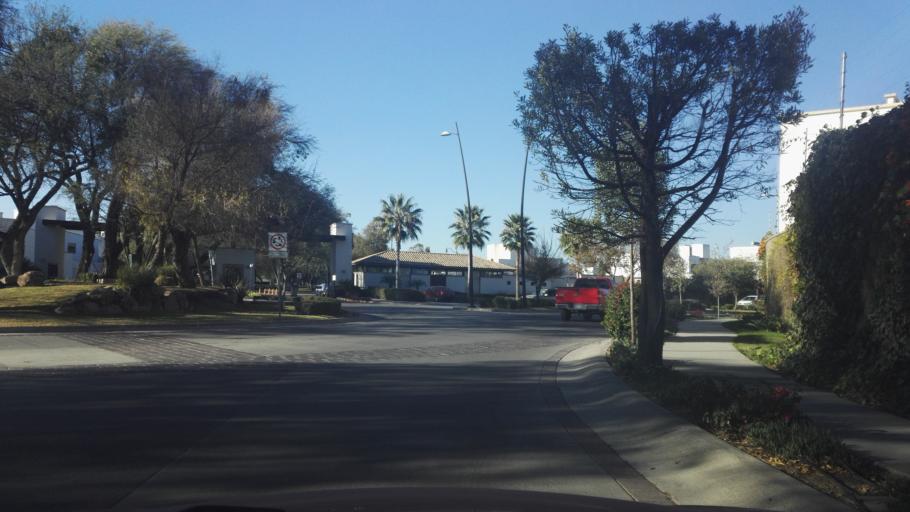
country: MX
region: Guanajuato
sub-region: Leon
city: Ladrilleras del Refugio
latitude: 21.0646
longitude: -101.5980
